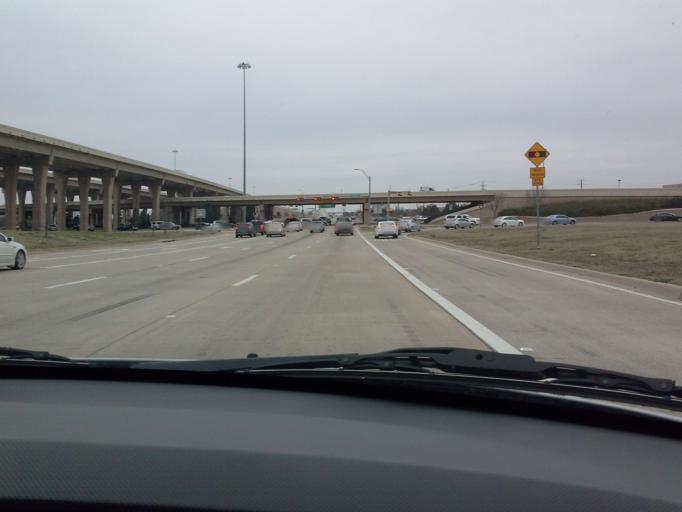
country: US
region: Texas
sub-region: Collin County
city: Frisco
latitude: 33.0984
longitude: -96.8041
